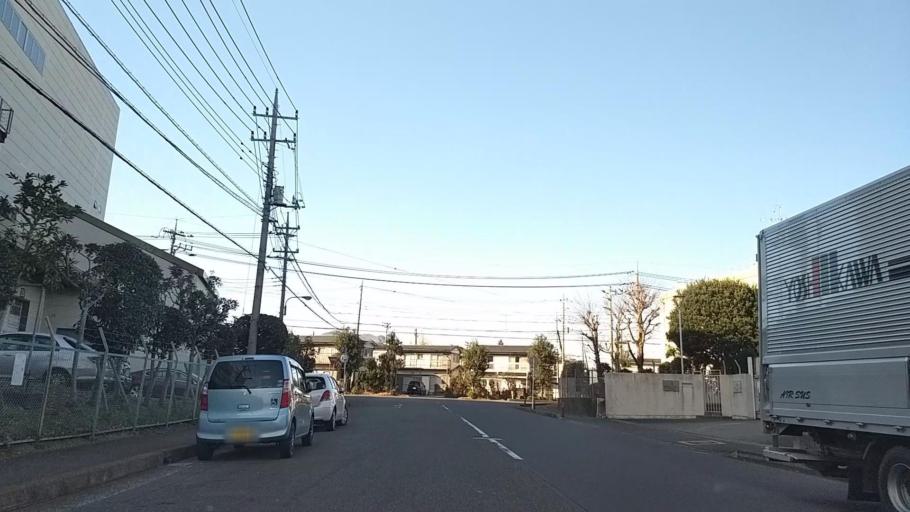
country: JP
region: Kanagawa
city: Atsugi
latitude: 35.4608
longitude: 139.3257
